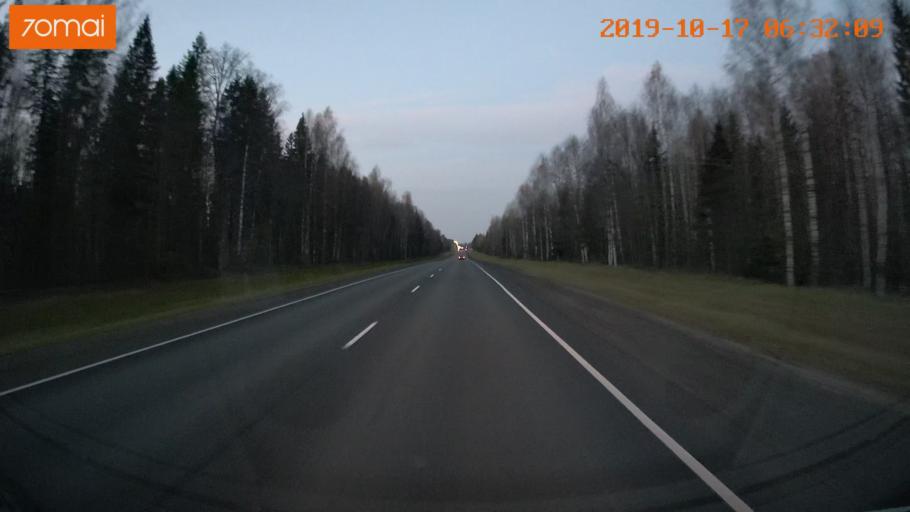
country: RU
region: Ivanovo
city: Novoye Leushino
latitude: 56.7222
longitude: 40.6833
